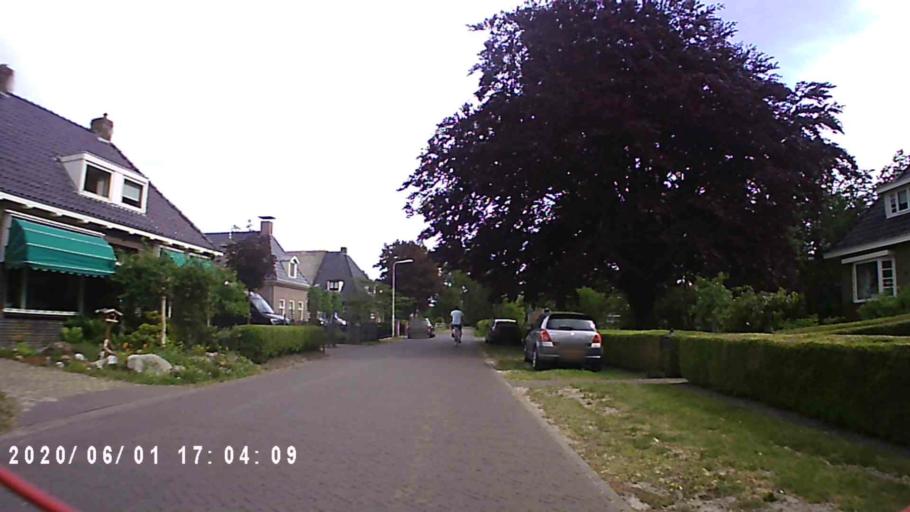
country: NL
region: Friesland
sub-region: Gemeente Tytsjerksteradiel
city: Garyp
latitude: 53.1752
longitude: 5.9329
